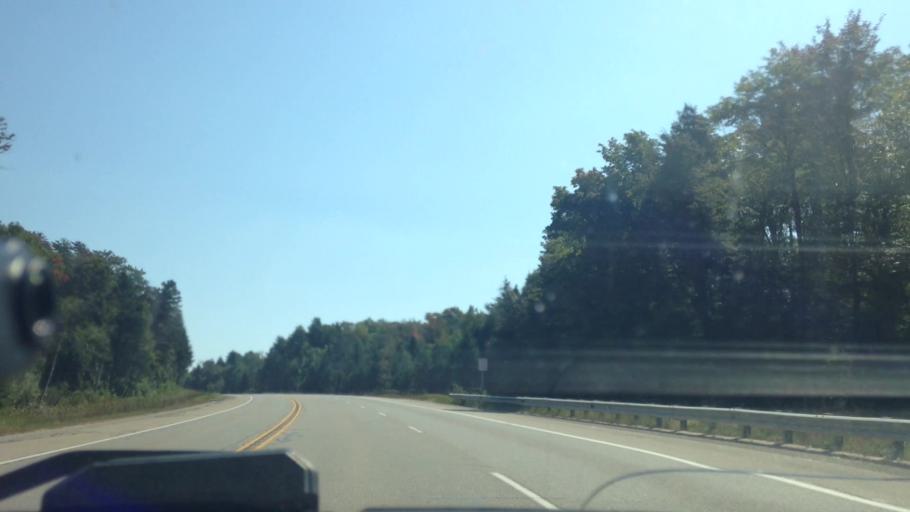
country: US
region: Michigan
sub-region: Alger County
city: Munising
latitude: 46.3894
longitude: -86.6461
